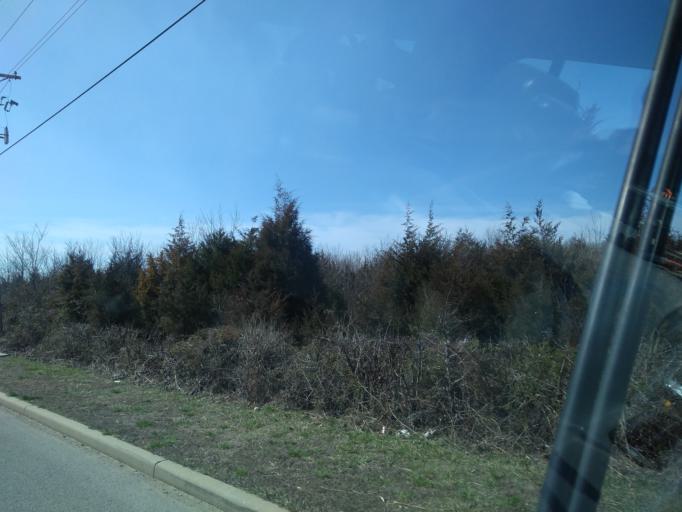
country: US
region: Arkansas
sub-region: Washington County
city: Farmington
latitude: 36.0546
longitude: -94.2359
